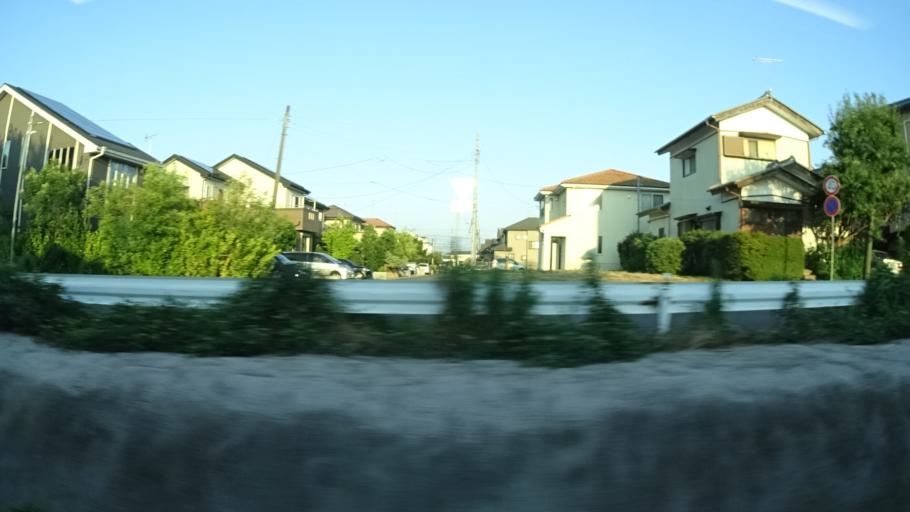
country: JP
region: Ibaraki
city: Ushiku
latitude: 35.9863
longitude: 140.1452
